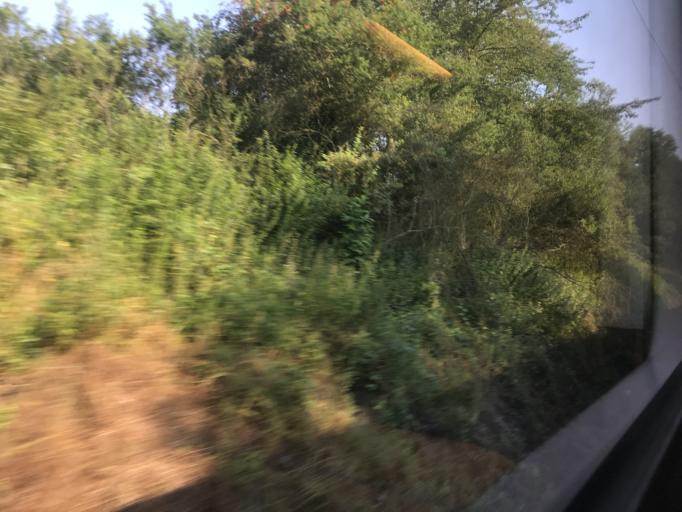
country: CZ
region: Central Bohemia
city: Votice
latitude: 49.6230
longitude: 14.6007
